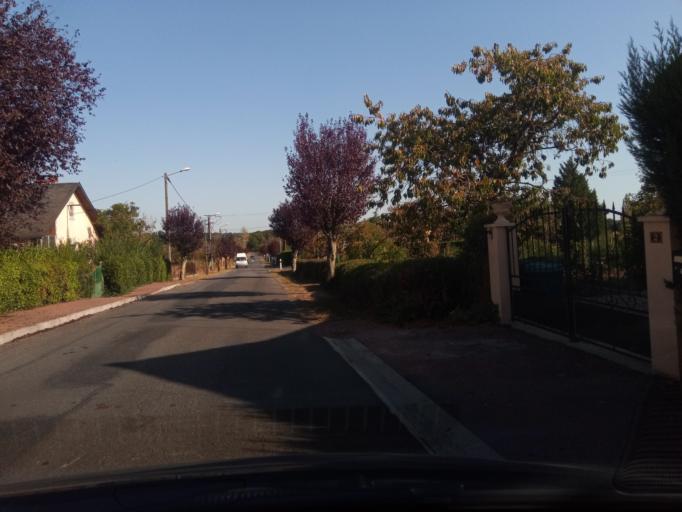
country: FR
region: Poitou-Charentes
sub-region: Departement de la Vienne
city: Saulge
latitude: 46.3337
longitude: 0.8731
